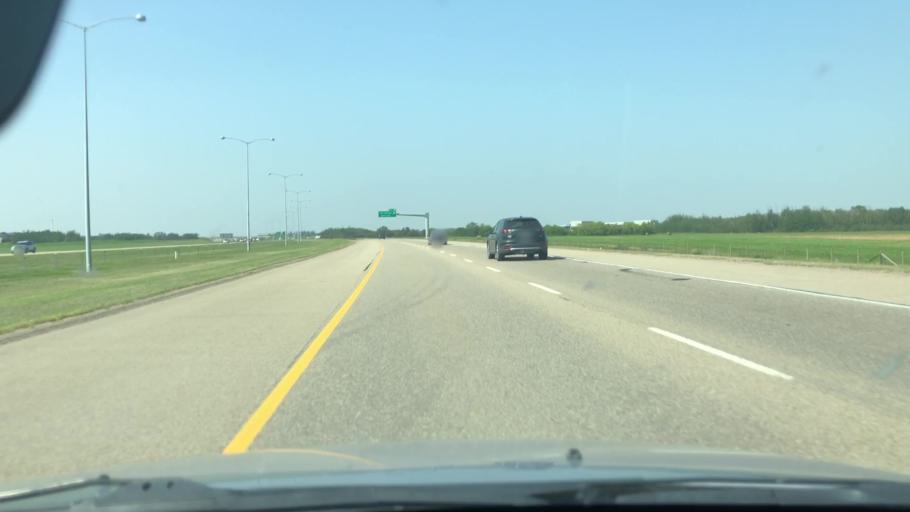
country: CA
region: Alberta
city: Edmonton
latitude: 53.6461
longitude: -113.5209
